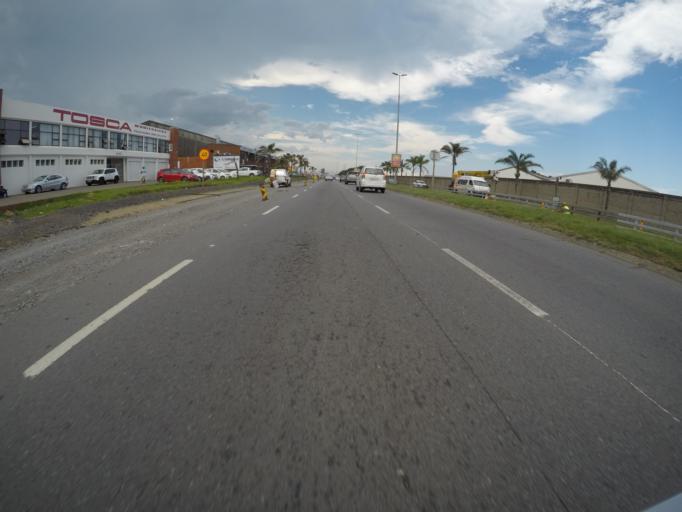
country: ZA
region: Eastern Cape
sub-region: Buffalo City Metropolitan Municipality
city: East London
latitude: -33.0293
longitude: 27.8873
